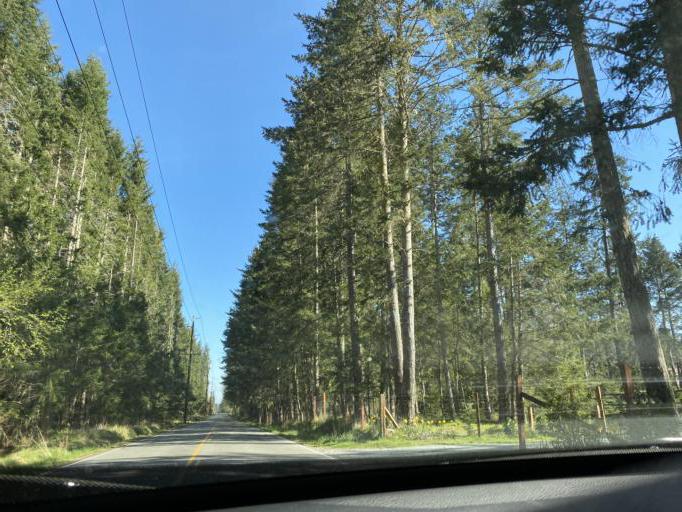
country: US
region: Washington
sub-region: Island County
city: Freeland
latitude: 48.0835
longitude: -122.5830
